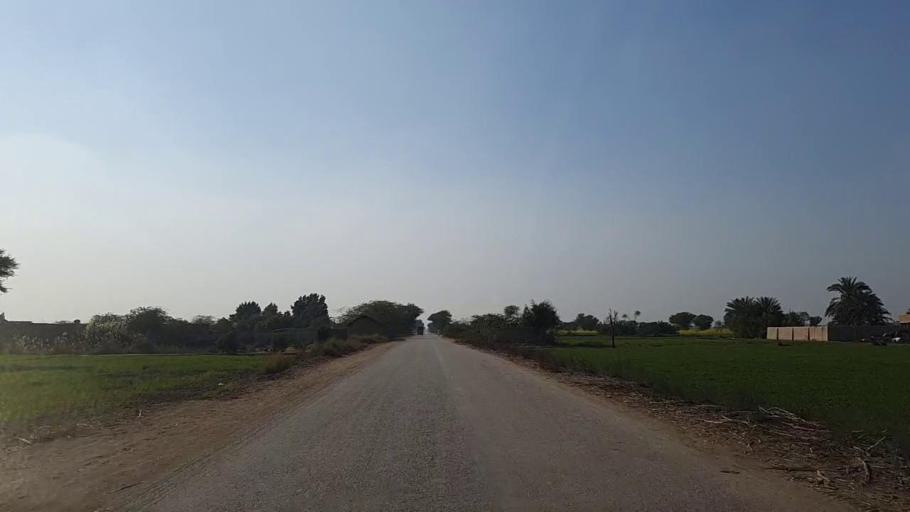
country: PK
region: Sindh
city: Daur
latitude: 26.4039
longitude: 68.3081
